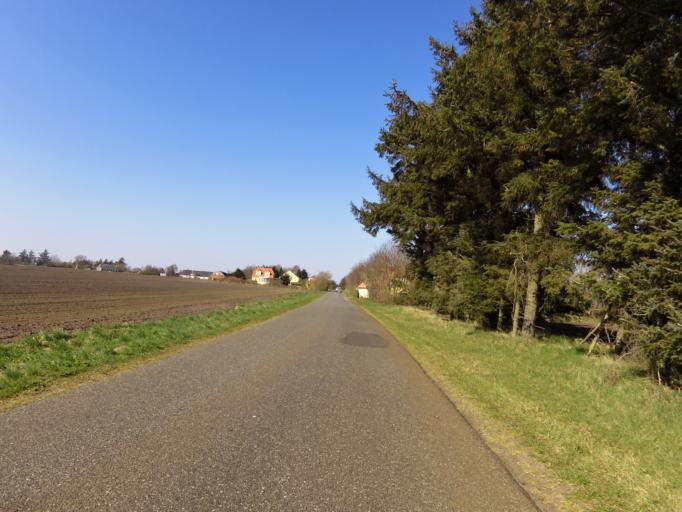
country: DK
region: South Denmark
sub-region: Esbjerg Kommune
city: Ribe
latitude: 55.3636
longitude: 8.8066
